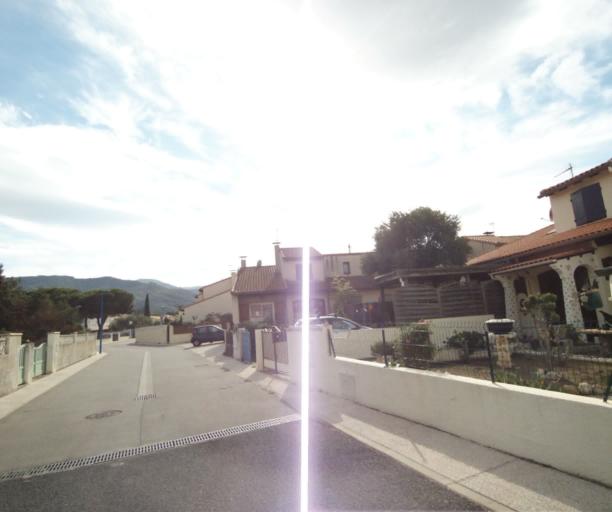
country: FR
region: Languedoc-Roussillon
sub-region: Departement des Pyrenees-Orientales
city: Argelers
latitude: 42.5479
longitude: 3.0130
